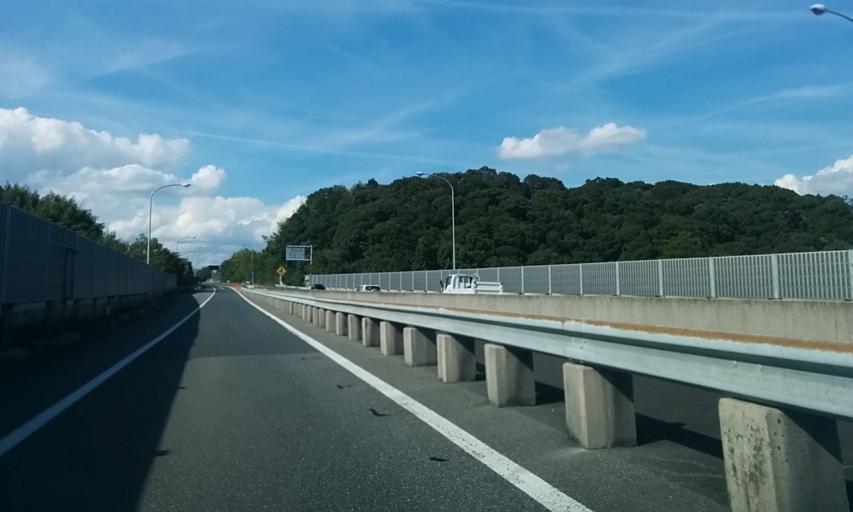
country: JP
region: Nara
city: Nara-shi
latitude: 34.7379
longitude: 135.7906
